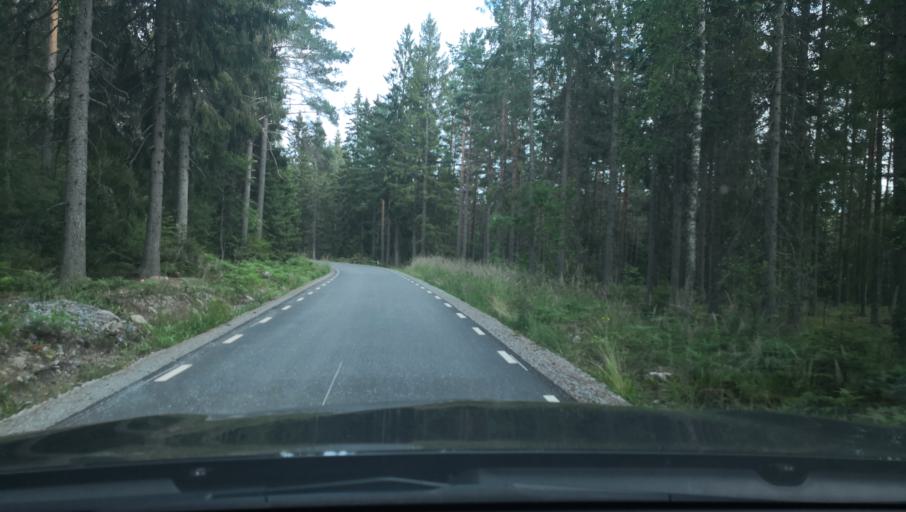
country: SE
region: Vaestmanland
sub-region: Surahammars Kommun
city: Surahammar
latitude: 59.6735
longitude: 16.1211
